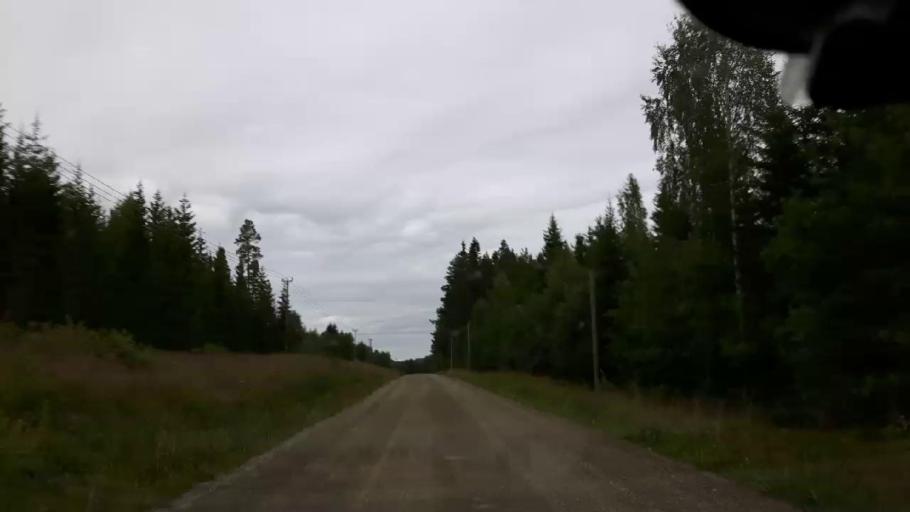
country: SE
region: Jaemtland
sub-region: Braecke Kommun
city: Braecke
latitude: 63.0243
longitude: 15.3724
